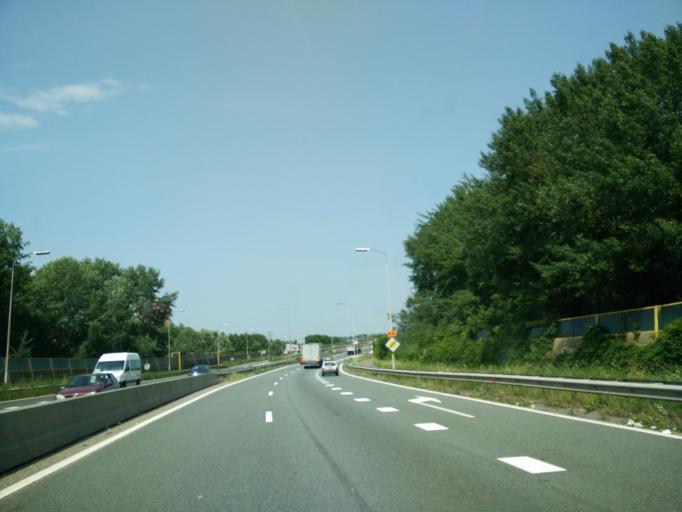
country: NL
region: South Holland
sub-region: Gemeente Papendrecht
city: Papendrecht
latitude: 51.8279
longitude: 4.7052
